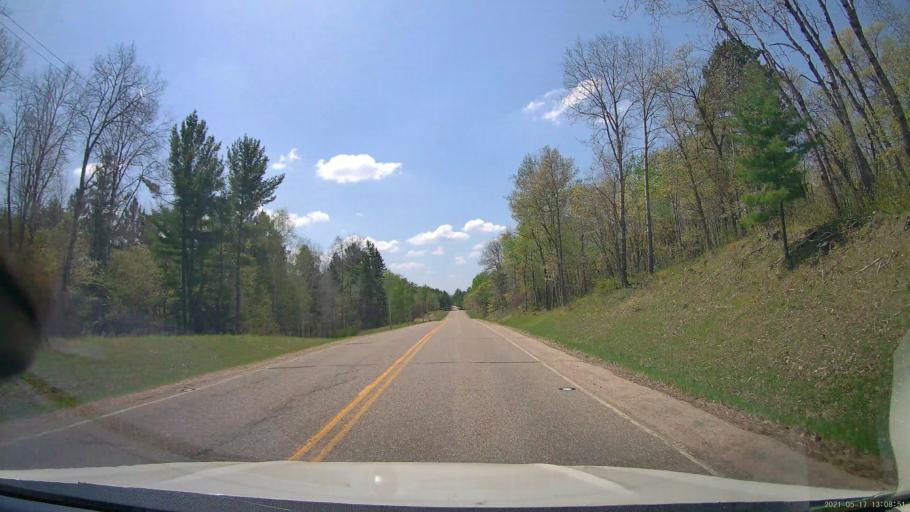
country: US
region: Minnesota
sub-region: Hubbard County
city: Park Rapids
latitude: 47.0329
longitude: -94.9209
